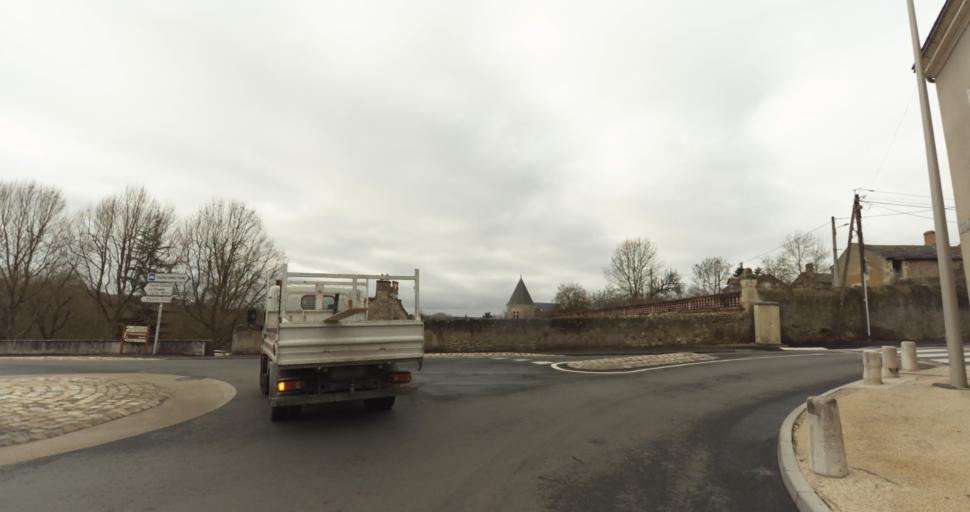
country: FR
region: Pays de la Loire
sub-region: Departement de Maine-et-Loire
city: Montreuil-Bellay
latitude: 47.1373
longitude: -0.1562
